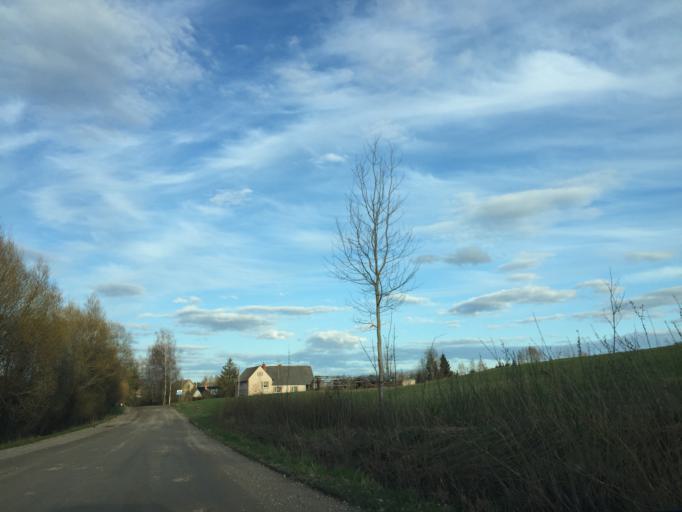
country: LV
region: Rezekne
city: Rezekne
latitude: 56.5725
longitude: 27.3552
